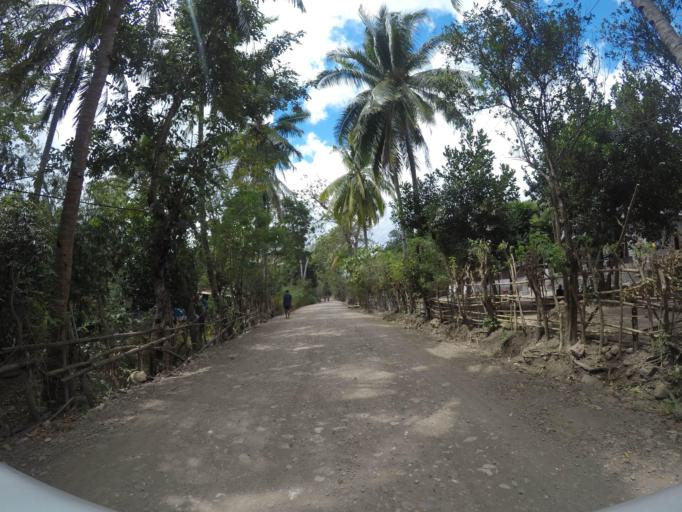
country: TL
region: Lautem
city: Lospalos
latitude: -8.5162
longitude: 126.8356
